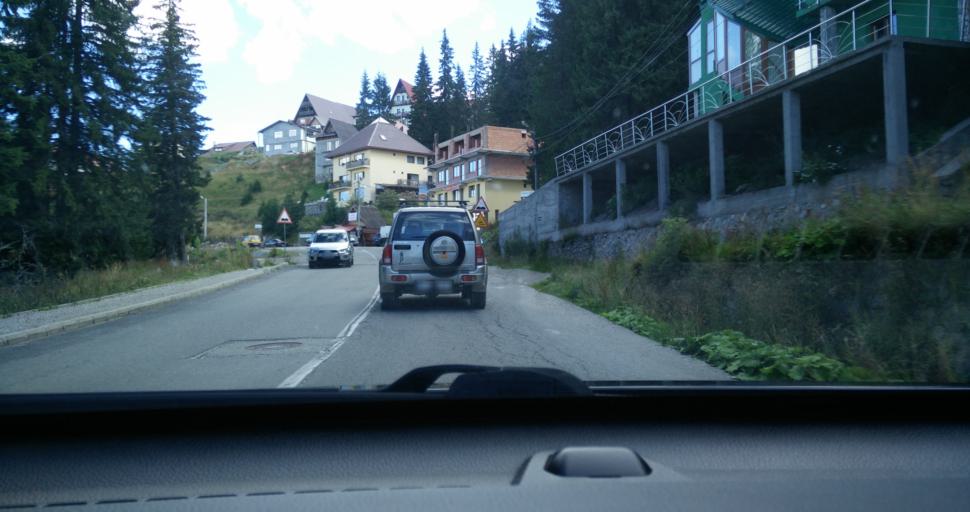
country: RO
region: Gorj
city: Novaci-Straini
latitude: 45.2863
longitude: 23.6922
